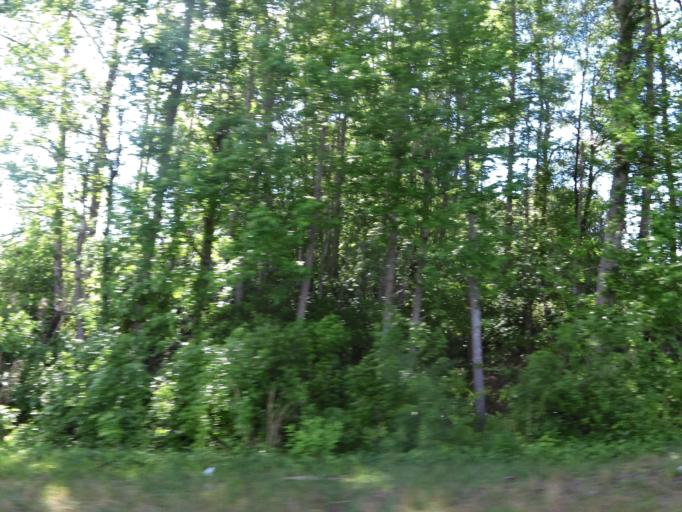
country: US
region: South Carolina
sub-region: Allendale County
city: Allendale
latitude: 33.0790
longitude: -81.2106
